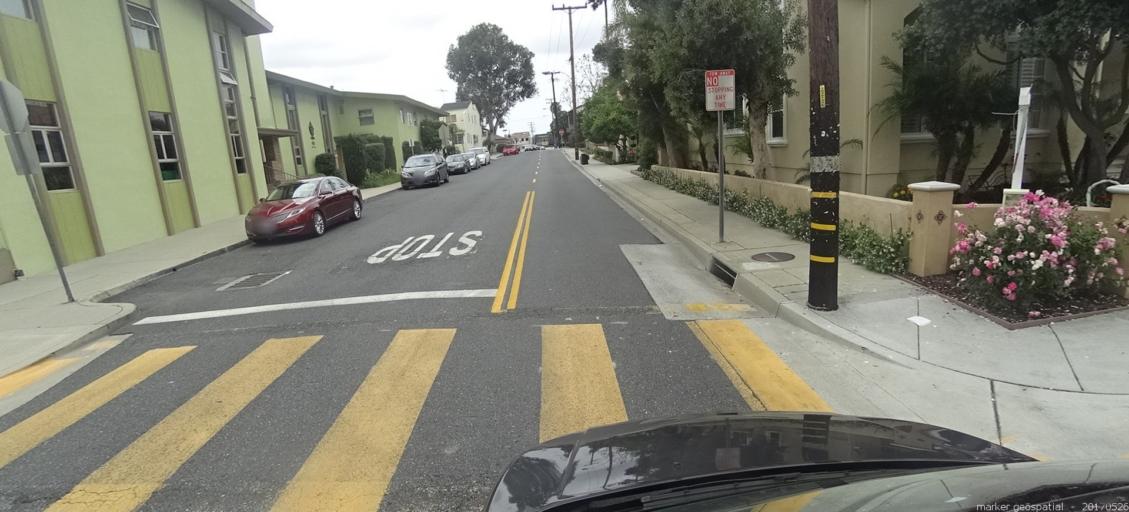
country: US
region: California
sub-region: Los Angeles County
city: Lawndale
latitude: 33.8747
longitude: -118.3700
